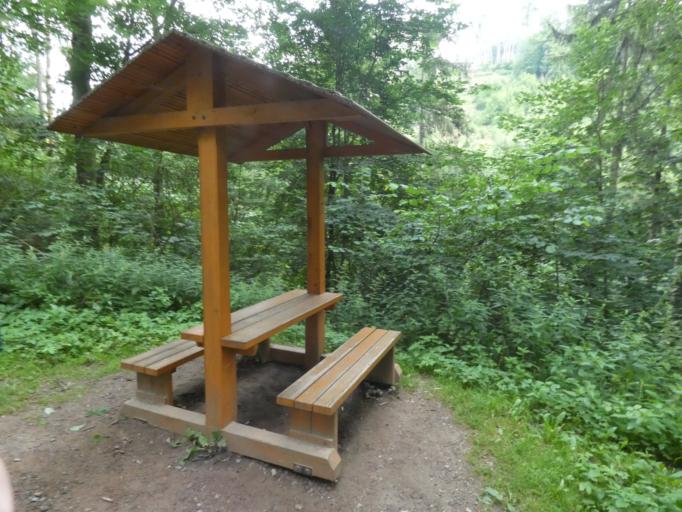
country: CZ
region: South Moravian
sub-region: Okres Brno-Venkov
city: Nedvedice
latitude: 49.4520
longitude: 16.3184
